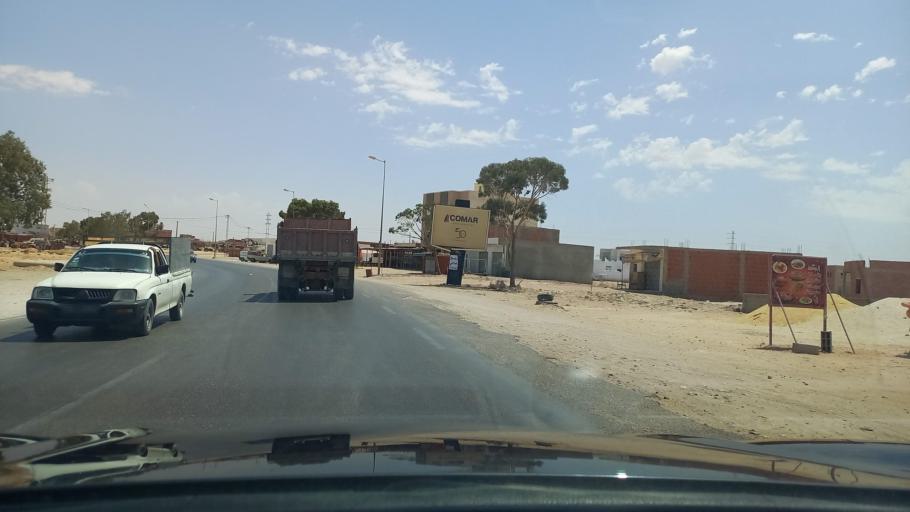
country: TN
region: Madanin
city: Medenine
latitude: 33.3691
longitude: 10.4495
